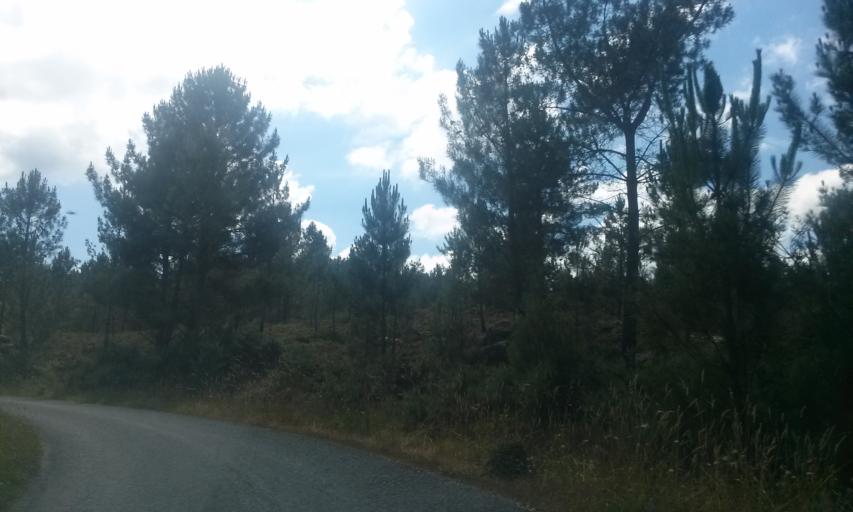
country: ES
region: Galicia
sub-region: Provincia de Lugo
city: Begonte
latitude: 43.1197
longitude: -7.6751
